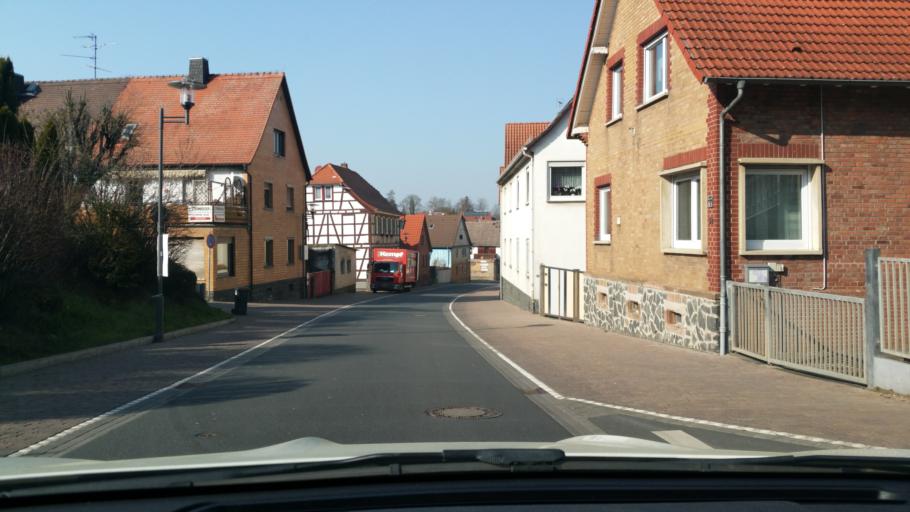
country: DE
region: Hesse
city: Reinheim
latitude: 49.8407
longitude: 8.8277
